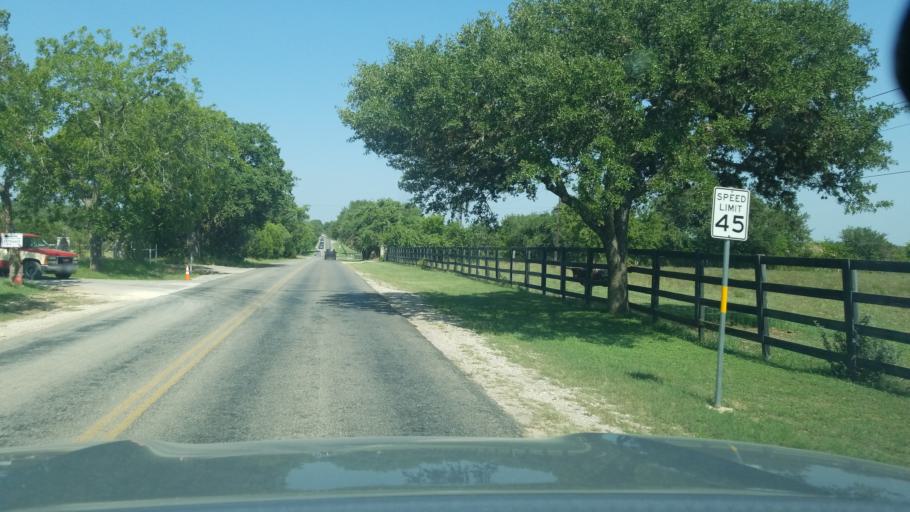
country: US
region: Texas
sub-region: Bexar County
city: Fair Oaks Ranch
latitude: 29.7868
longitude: -98.6762
